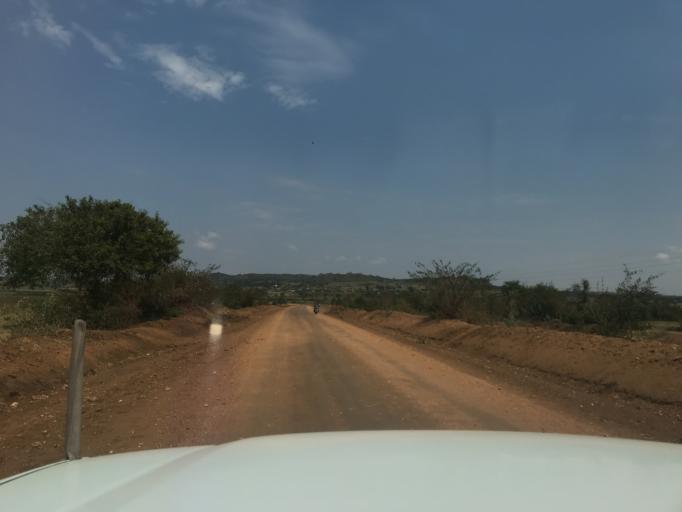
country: TZ
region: Mara
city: Nyamuswa
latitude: -1.9733
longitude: 33.9718
